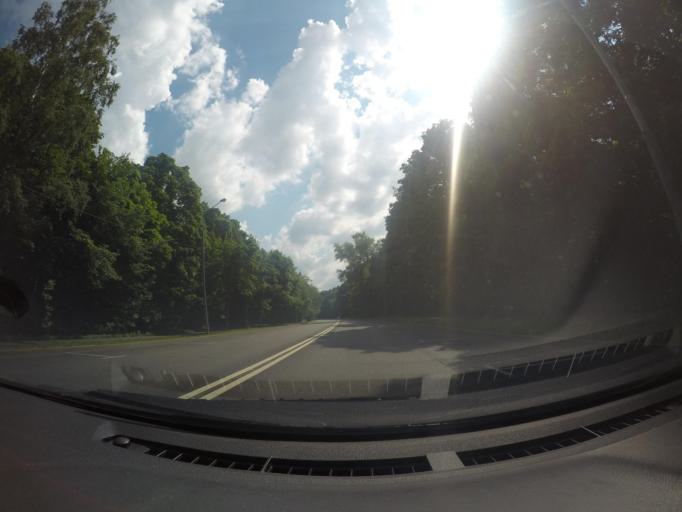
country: RU
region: Moscow
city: Sokol'niki
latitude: 55.8101
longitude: 37.6846
